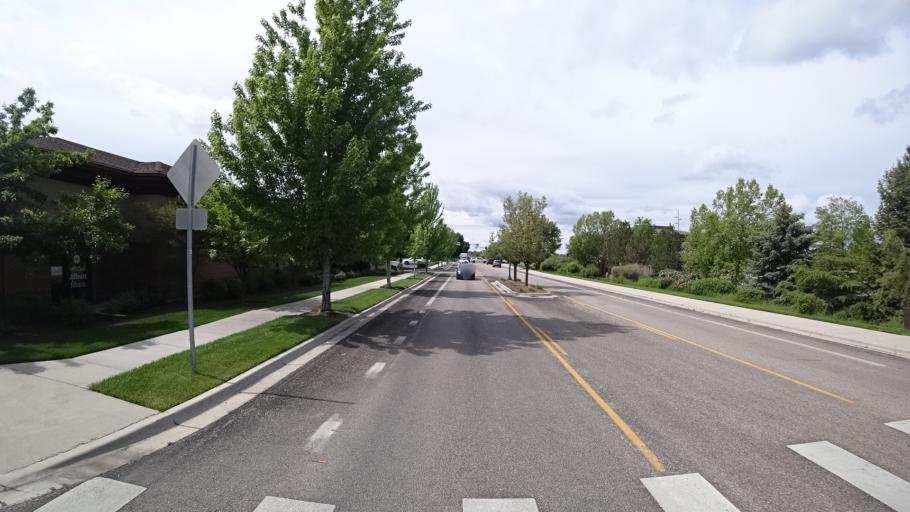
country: US
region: Idaho
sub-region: Ada County
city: Eagle
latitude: 43.6943
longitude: -116.3397
